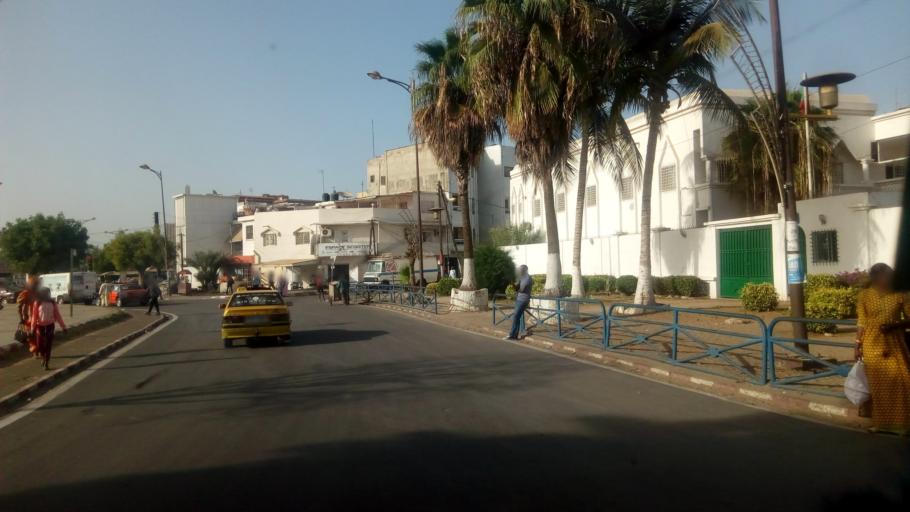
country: SN
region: Dakar
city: Dakar
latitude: 14.6908
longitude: -17.4468
